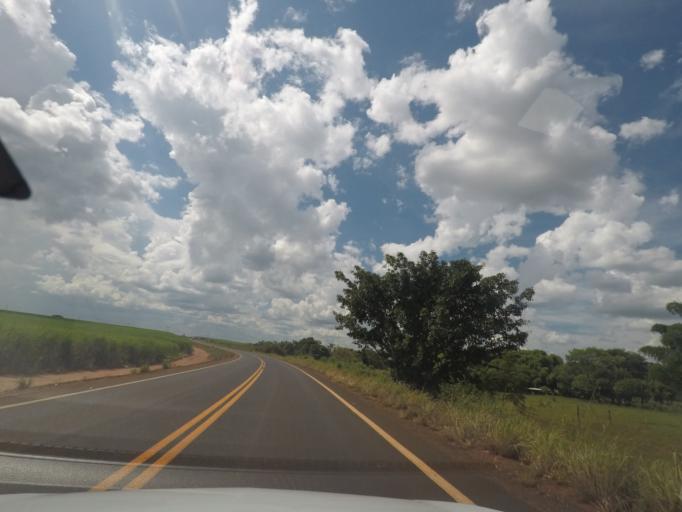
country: BR
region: Minas Gerais
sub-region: Conceicao Das Alagoas
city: Conceicao das Alagoas
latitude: -19.8339
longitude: -48.5898
